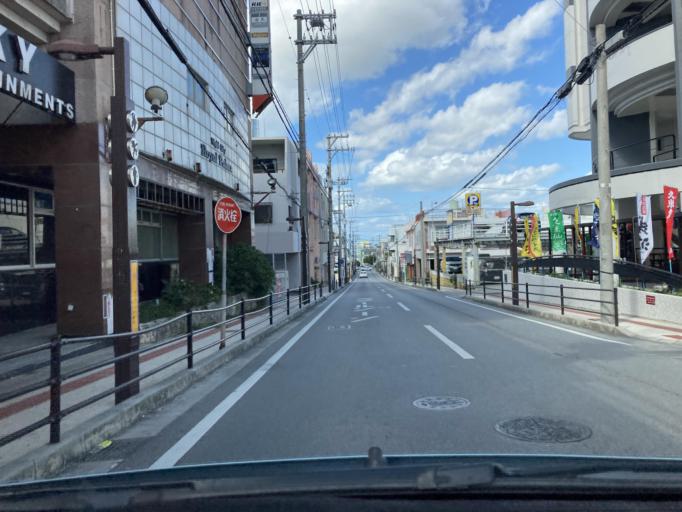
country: JP
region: Okinawa
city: Okinawa
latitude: 26.3306
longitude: 127.7949
